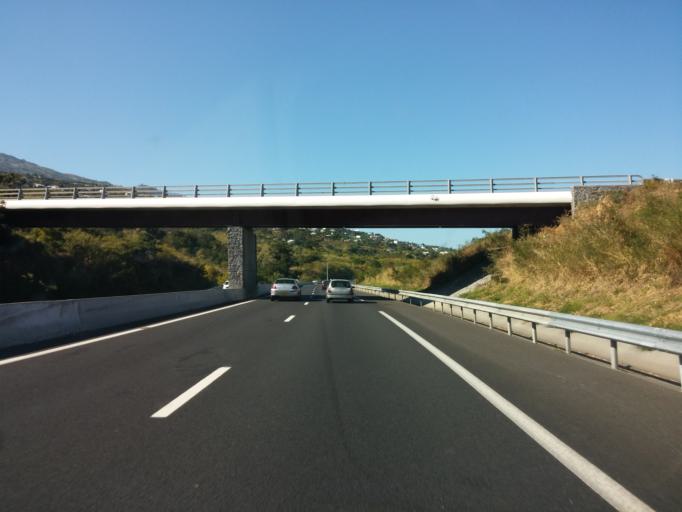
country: RE
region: Reunion
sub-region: Reunion
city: Saint-Leu
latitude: -21.1599
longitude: 55.2961
